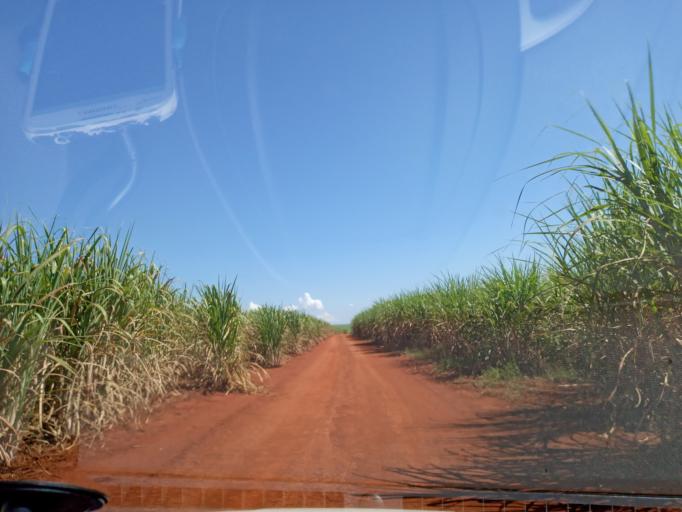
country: BR
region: Goias
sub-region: Itumbiara
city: Itumbiara
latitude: -18.4406
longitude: -49.1463
